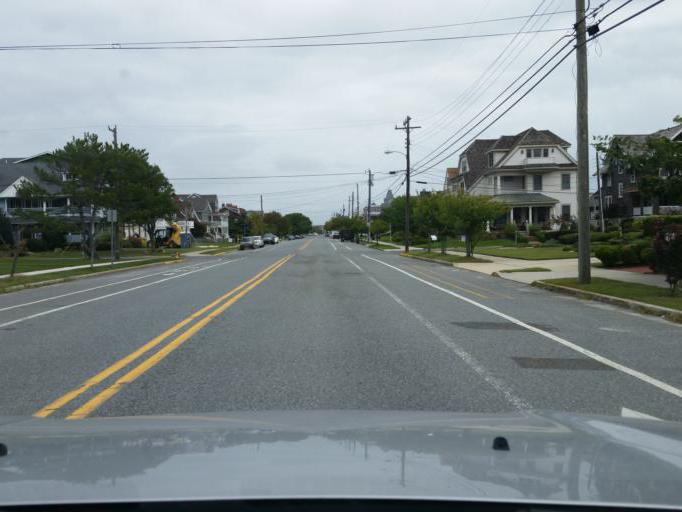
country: US
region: New Jersey
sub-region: Cape May County
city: Cape May
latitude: 38.9341
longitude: -74.9067
